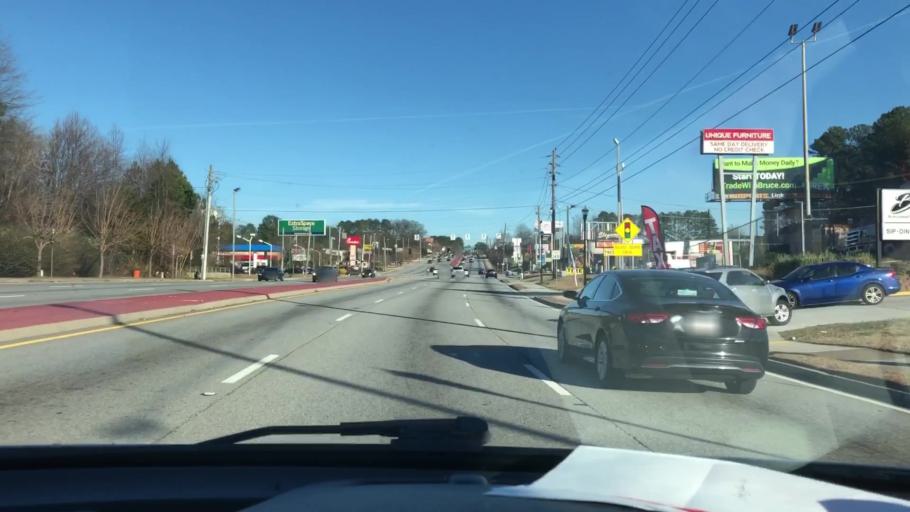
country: US
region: Georgia
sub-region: DeKalb County
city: Clarkston
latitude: 33.8005
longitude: -84.2143
